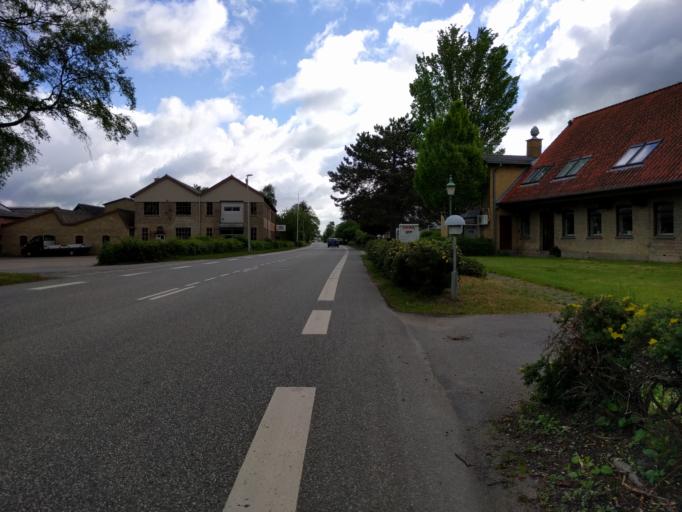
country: DK
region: South Denmark
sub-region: Kerteminde Kommune
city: Kerteminde
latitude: 55.4084
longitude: 10.6234
